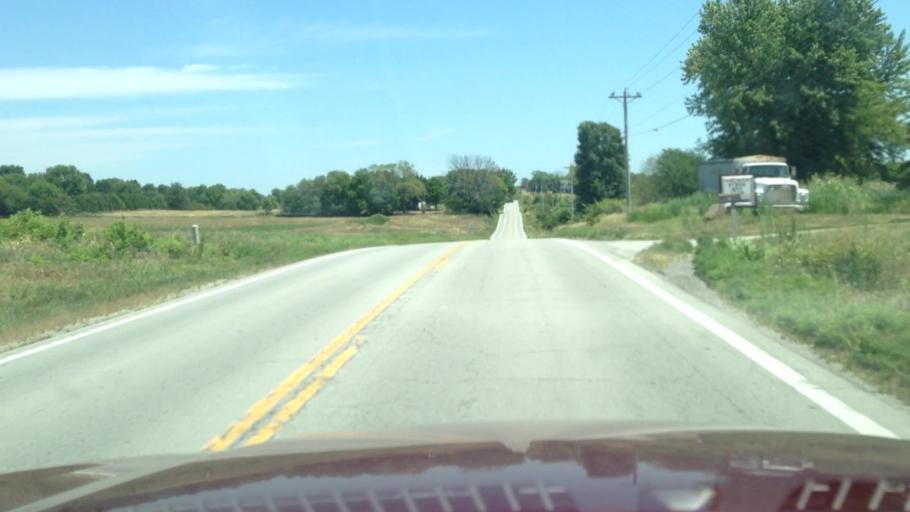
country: US
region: Missouri
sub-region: Clay County
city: Kearney
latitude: 39.3679
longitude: -94.4582
